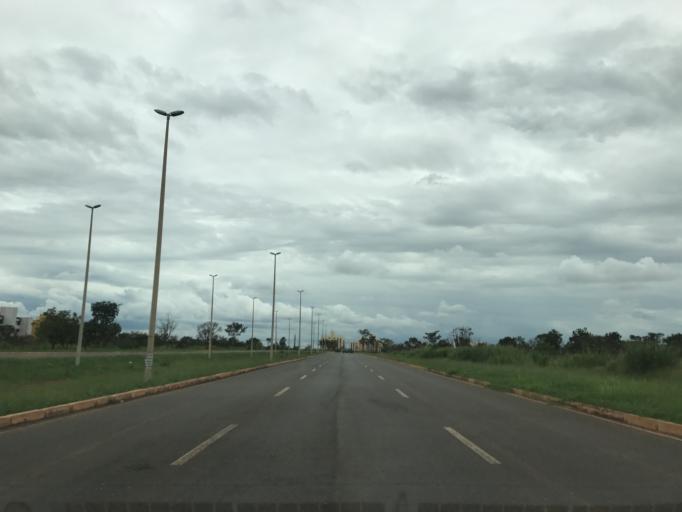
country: BR
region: Federal District
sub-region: Brasilia
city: Brasilia
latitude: -15.8061
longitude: -47.9922
